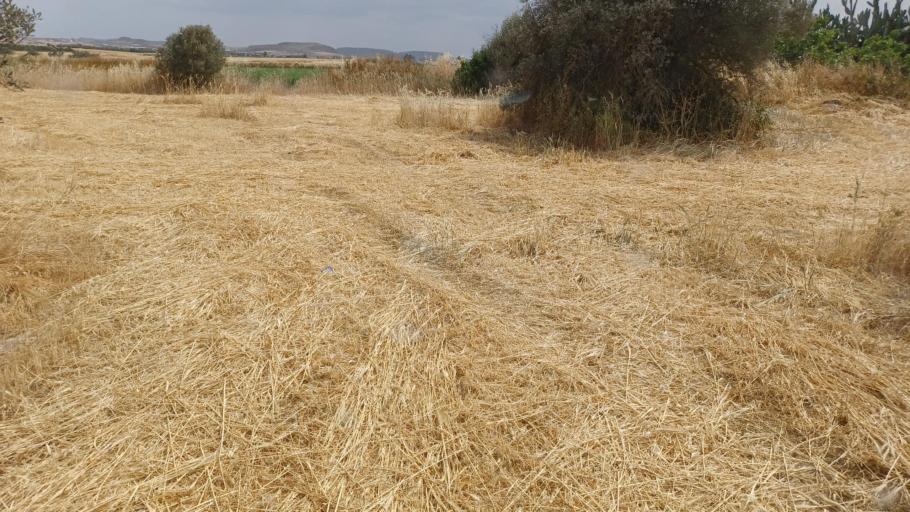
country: CY
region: Larnaka
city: Athienou
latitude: 35.0775
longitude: 33.5275
